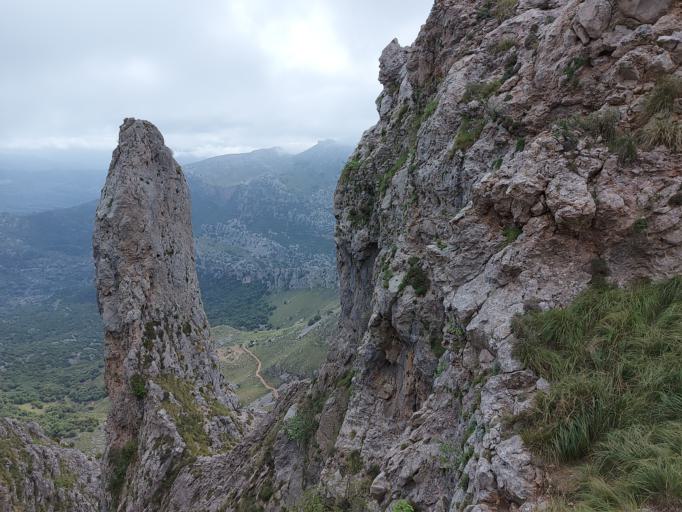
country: ES
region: Balearic Islands
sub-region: Illes Balears
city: Fornalutx
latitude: 39.8083
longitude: 2.8008
